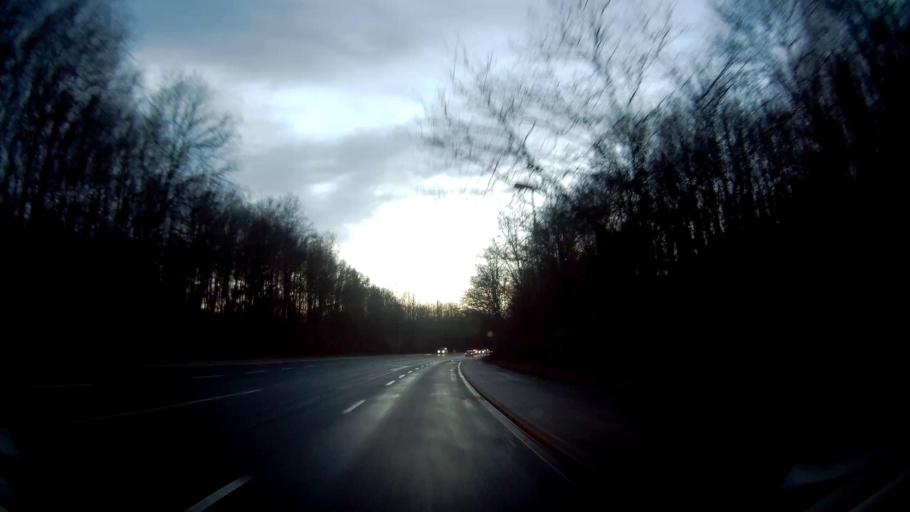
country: DE
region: North Rhine-Westphalia
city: Castrop-Rauxel
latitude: 51.4927
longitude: 7.2962
